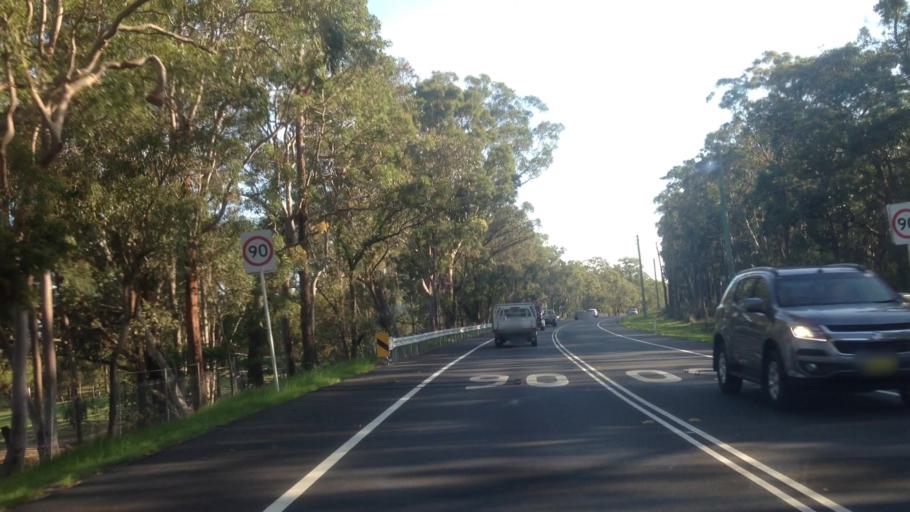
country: AU
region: New South Wales
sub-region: Lake Macquarie Shire
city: Dora Creek
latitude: -33.1188
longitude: 151.4781
